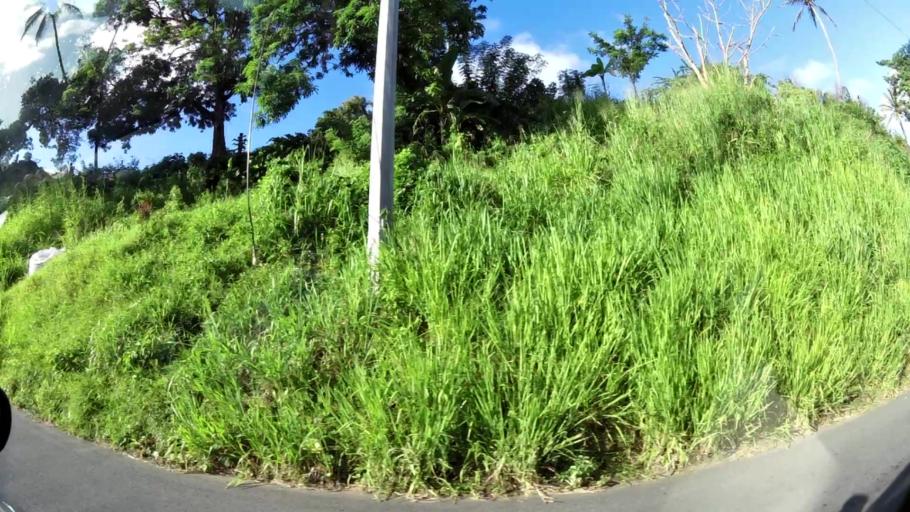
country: TT
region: Eastern Tobago
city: Roxborough
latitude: 11.2177
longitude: -60.6168
